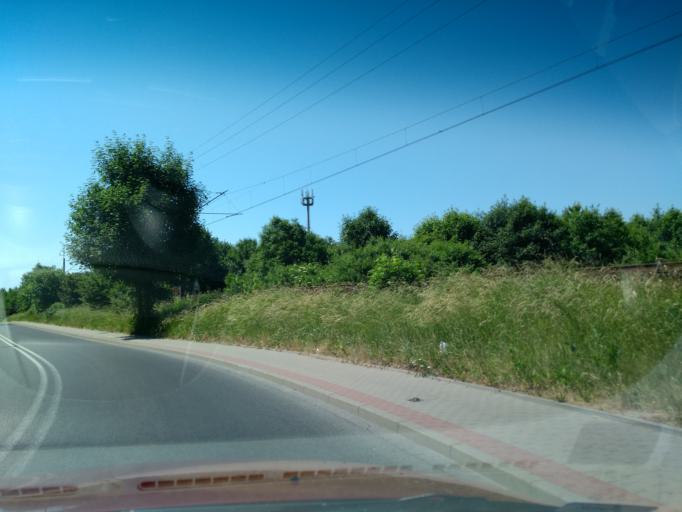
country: PL
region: West Pomeranian Voivodeship
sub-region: Koszalin
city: Koszalin
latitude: 54.2045
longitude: 16.1744
